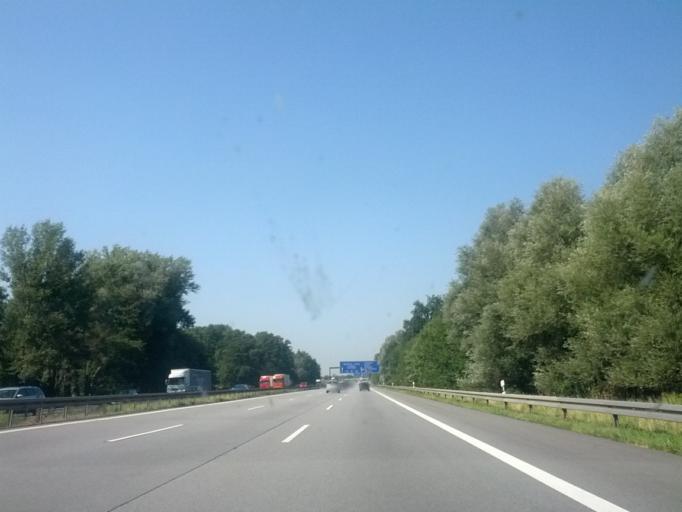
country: DE
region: Brandenburg
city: Rangsdorf
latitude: 52.3112
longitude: 13.4668
